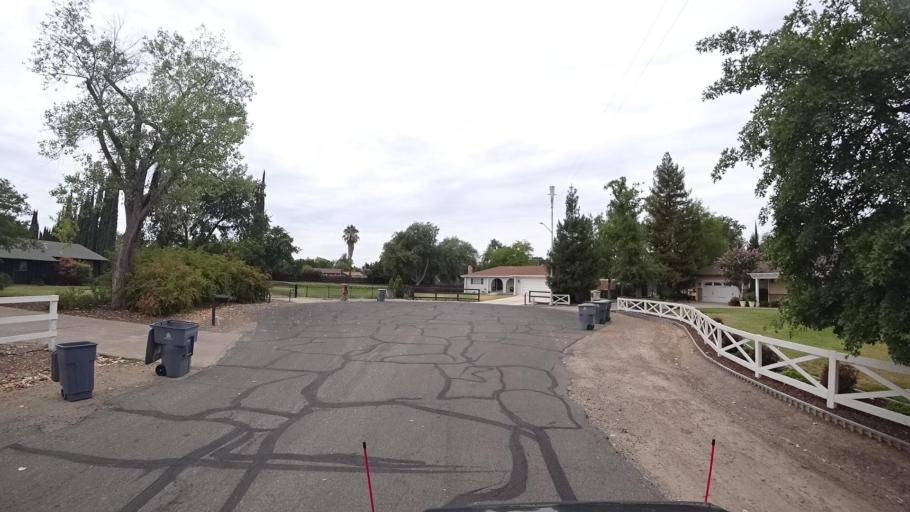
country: US
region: California
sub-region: Placer County
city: Rocklin
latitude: 38.7804
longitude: -121.2554
